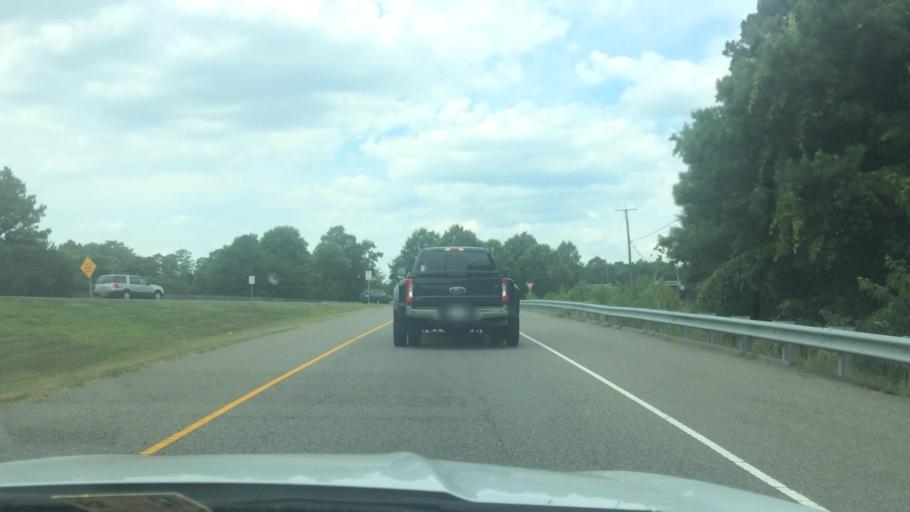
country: US
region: Virginia
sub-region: York County
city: Yorktown
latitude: 37.1733
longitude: -76.5666
